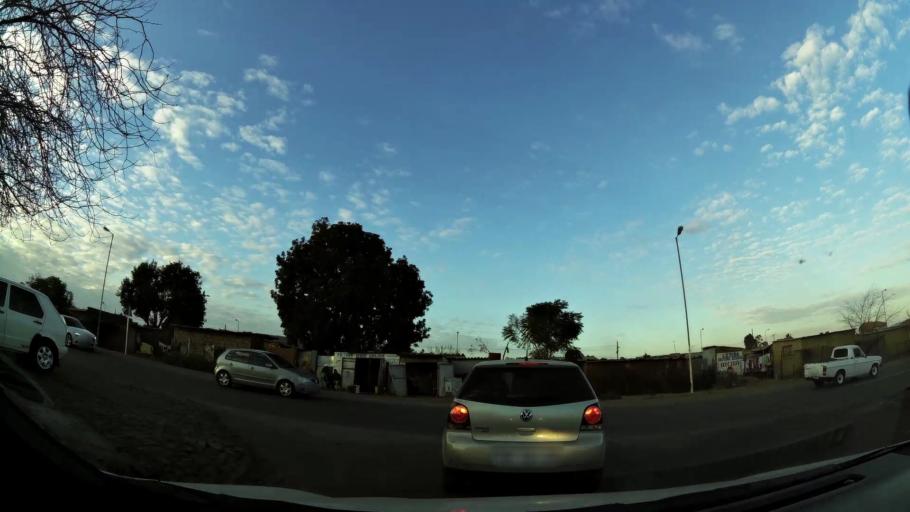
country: ZA
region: Gauteng
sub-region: City of Tshwane Metropolitan Municipality
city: Pretoria
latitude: -25.7151
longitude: 28.3552
